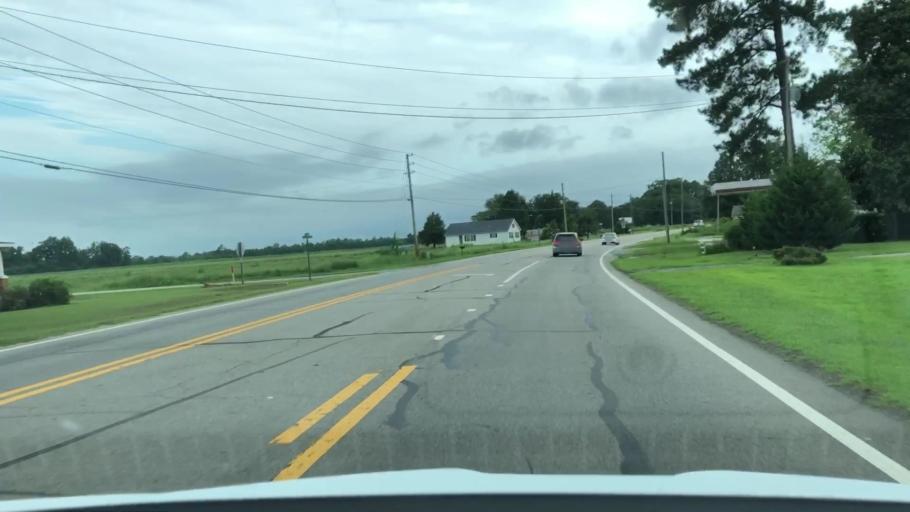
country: US
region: North Carolina
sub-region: Lenoir County
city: Kinston
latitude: 35.2081
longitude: -77.5664
